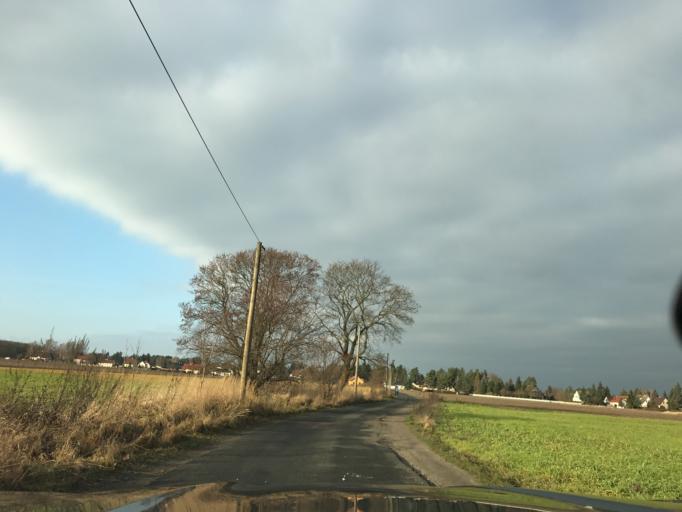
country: DE
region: Brandenburg
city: Brandenburg an der Havel
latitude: 52.3678
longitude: 12.5360
